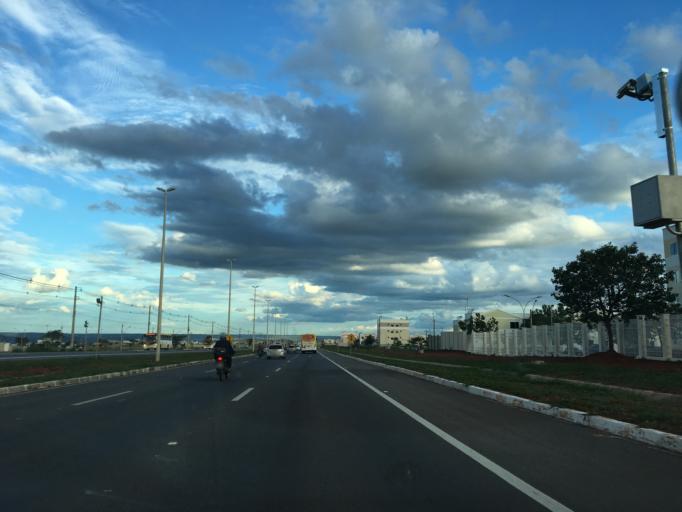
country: BR
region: Federal District
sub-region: Brasilia
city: Brasilia
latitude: -15.8869
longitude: -47.8113
